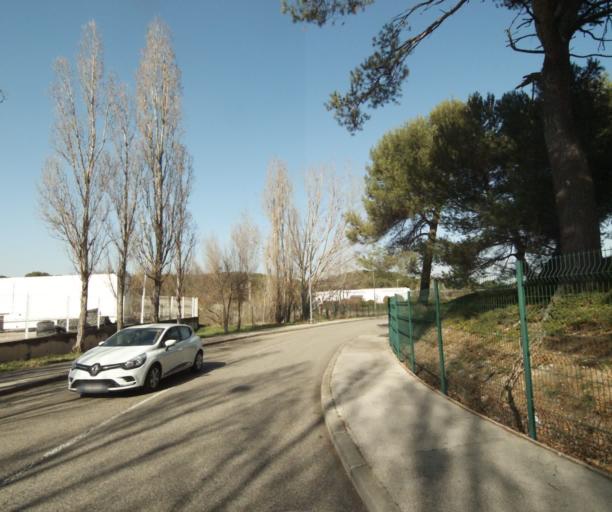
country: FR
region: Provence-Alpes-Cote d'Azur
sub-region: Departement des Bouches-du-Rhone
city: Cabries
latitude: 43.4281
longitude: 5.3946
